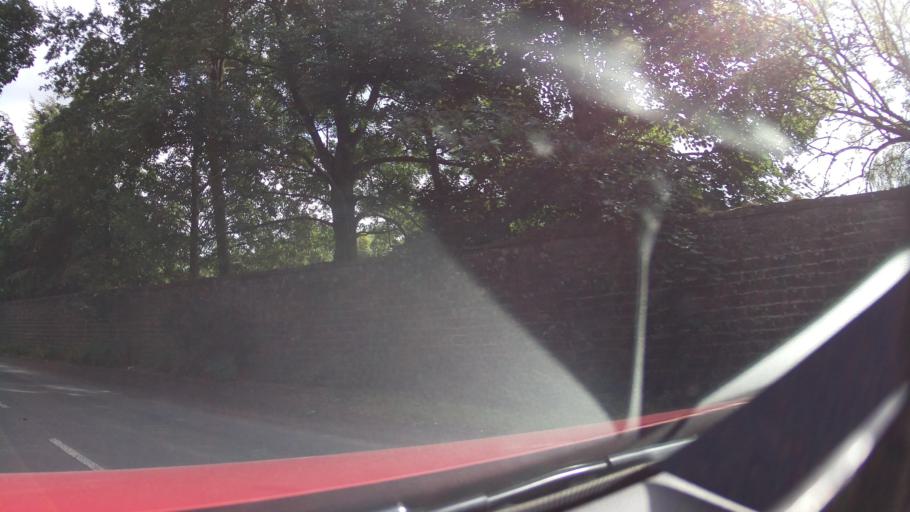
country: GB
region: England
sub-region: North Yorkshire
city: Leyburn
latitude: 54.2677
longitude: -1.7439
